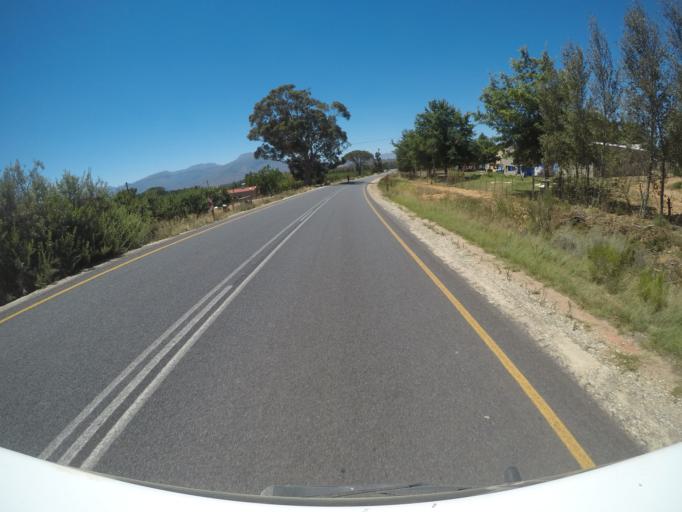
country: ZA
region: Western Cape
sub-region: Overberg District Municipality
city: Grabouw
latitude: -34.0589
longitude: 19.1382
